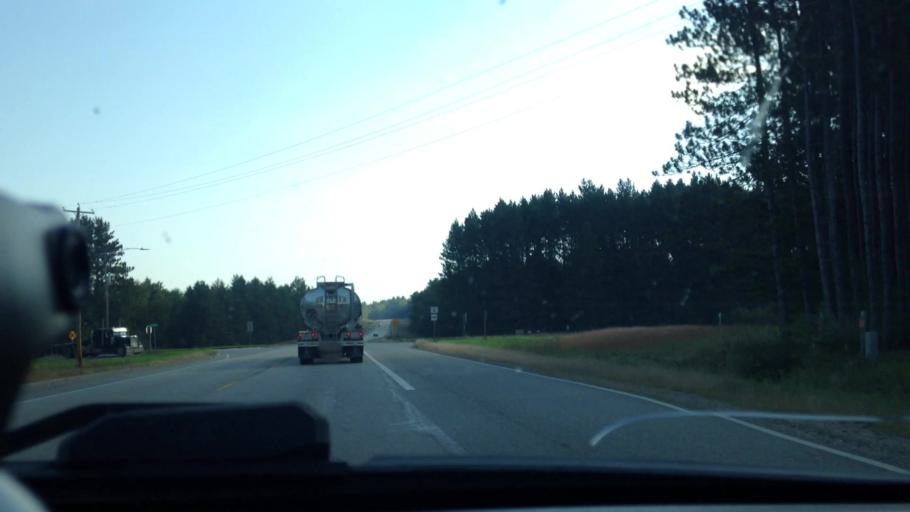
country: US
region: Wisconsin
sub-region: Marinette County
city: Niagara
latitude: 45.6395
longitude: -87.9807
